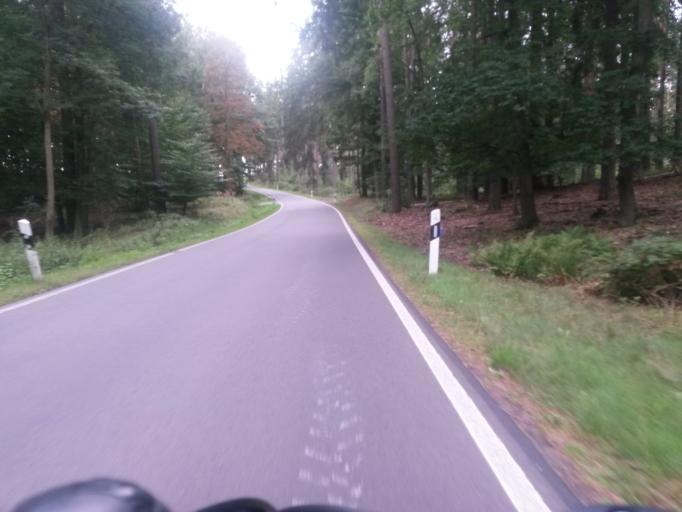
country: DE
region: Brandenburg
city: Angermunde
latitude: 53.0359
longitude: 13.9052
